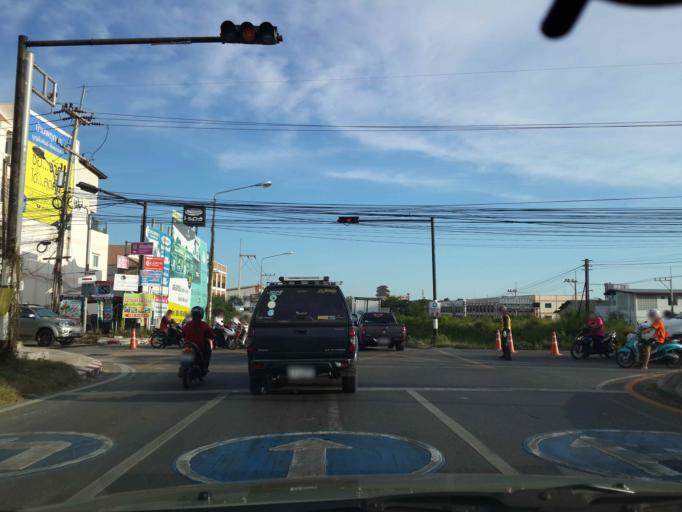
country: TH
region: Chon Buri
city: Phatthaya
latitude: 12.9258
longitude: 100.9034
